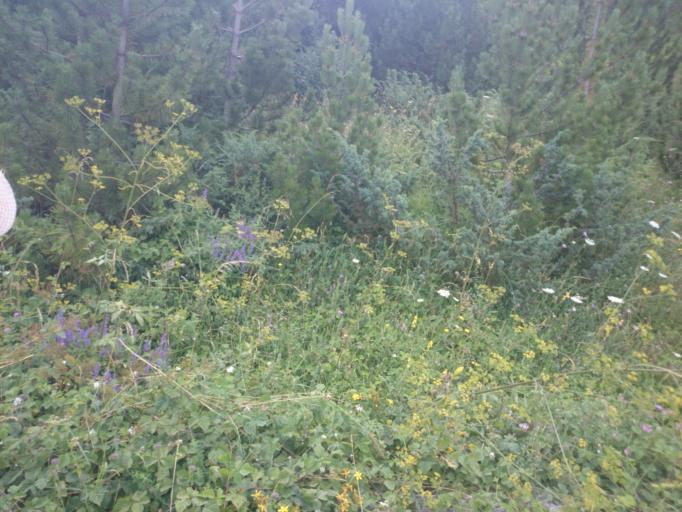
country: AL
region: Lezhe
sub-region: Rrethi i Mirdites
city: Orosh
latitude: 41.8652
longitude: 20.1198
